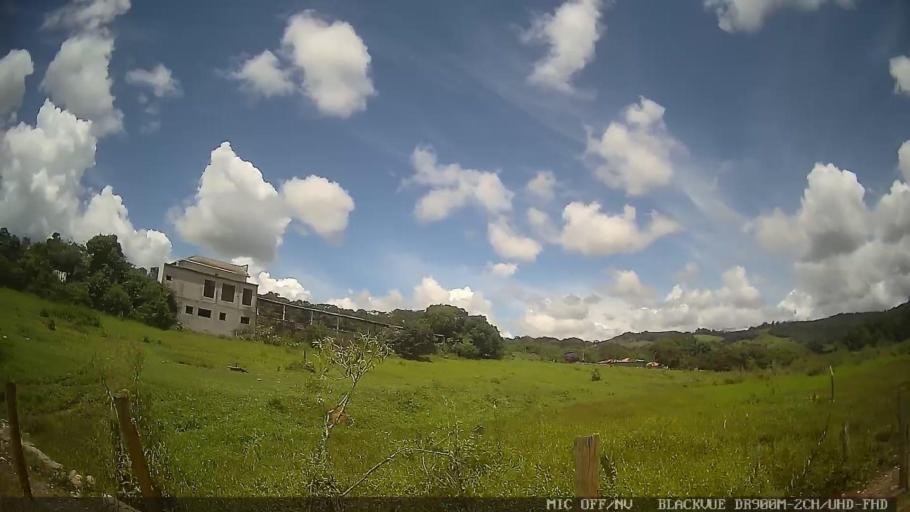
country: BR
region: Sao Paulo
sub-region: Amparo
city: Amparo
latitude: -22.8056
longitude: -46.7011
